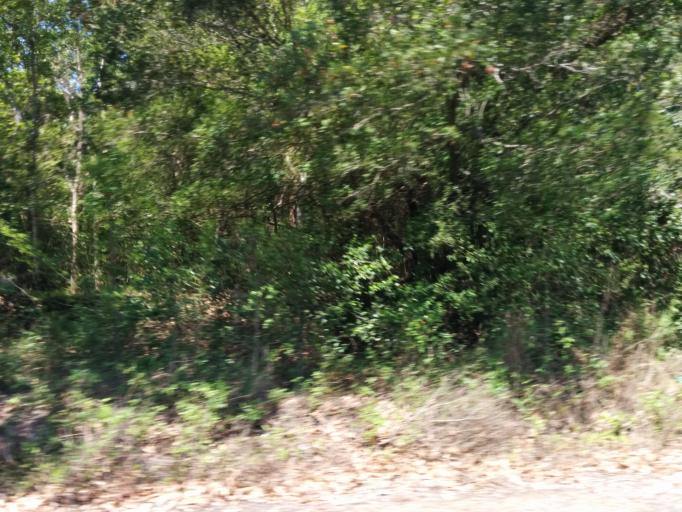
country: AU
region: Queensland
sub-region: Cairns
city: Palm Cove
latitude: -16.6797
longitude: 145.5738
